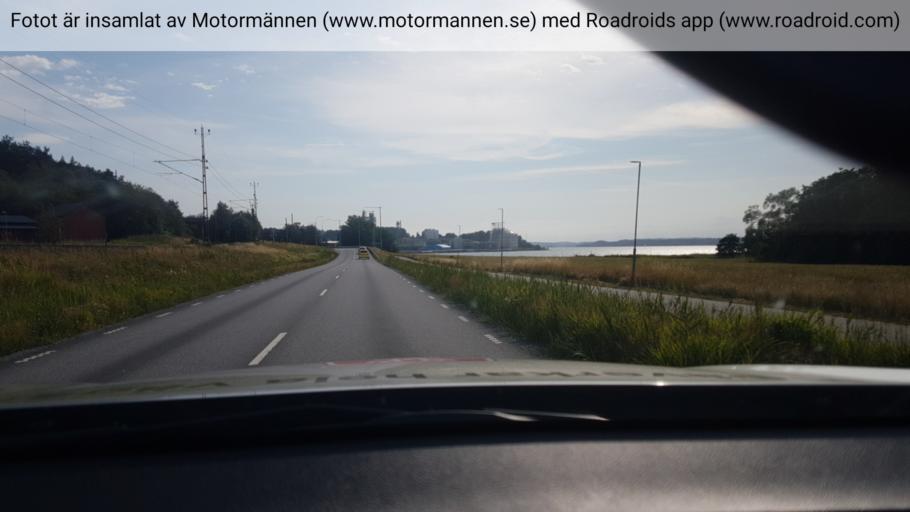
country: SE
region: Vaestra Goetaland
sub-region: Stenungsunds Kommun
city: Stenungsund
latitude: 58.0961
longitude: 11.8379
